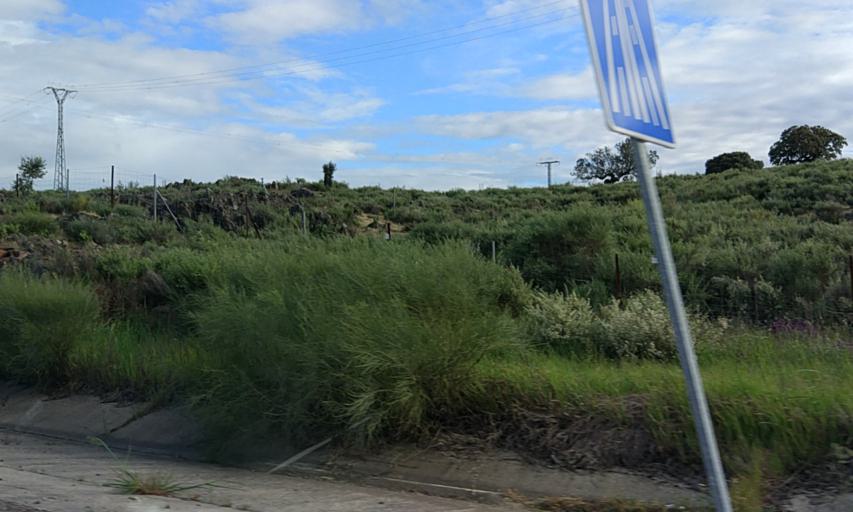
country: ES
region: Extremadura
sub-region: Provincia de Caceres
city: Casas de Don Gomez
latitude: 40.0265
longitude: -6.6076
